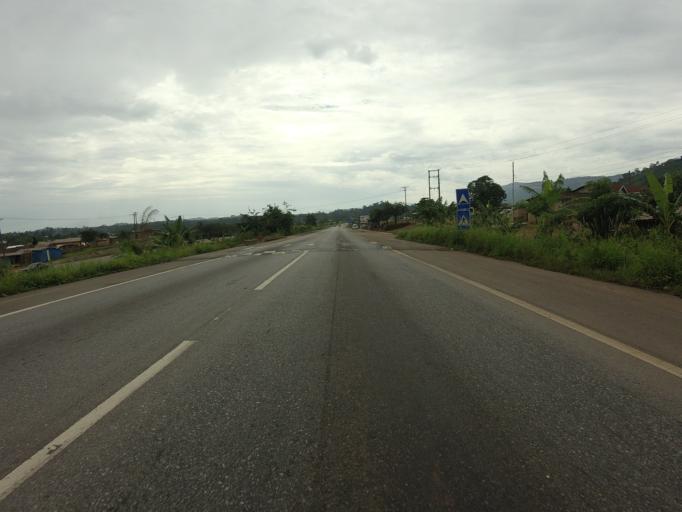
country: GH
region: Eastern
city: Nkawkaw
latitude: 6.5415
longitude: -0.7879
